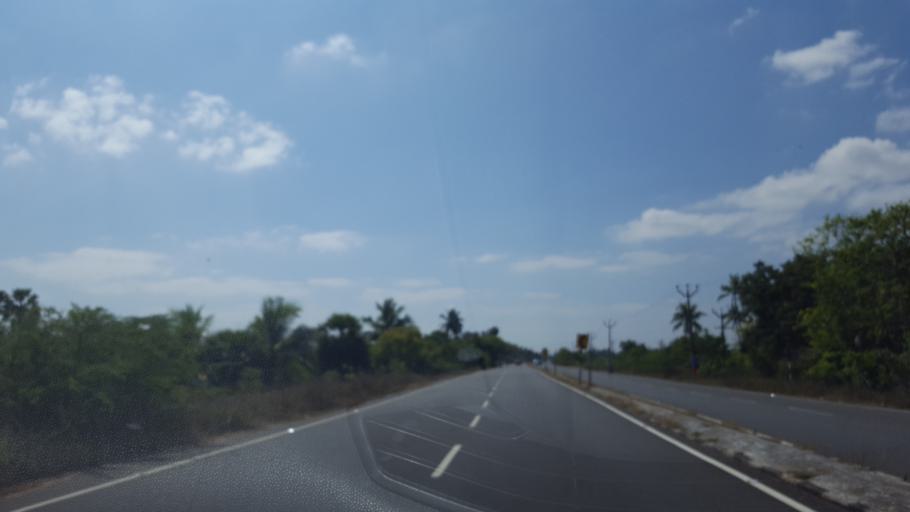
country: IN
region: Tamil Nadu
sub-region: Kancheepuram
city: Mamallapuram
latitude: 12.6357
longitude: 80.1719
